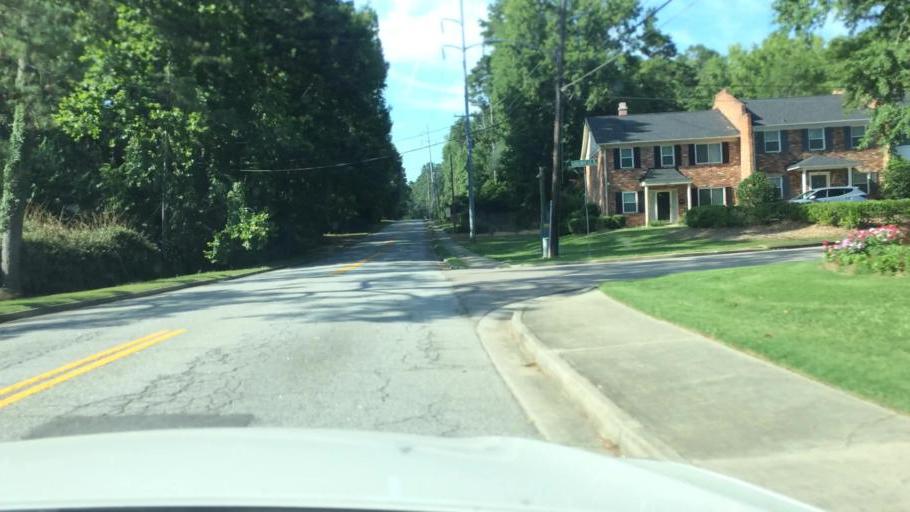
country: US
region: Georgia
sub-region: Columbia County
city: Martinez
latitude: 33.5029
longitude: -82.0399
